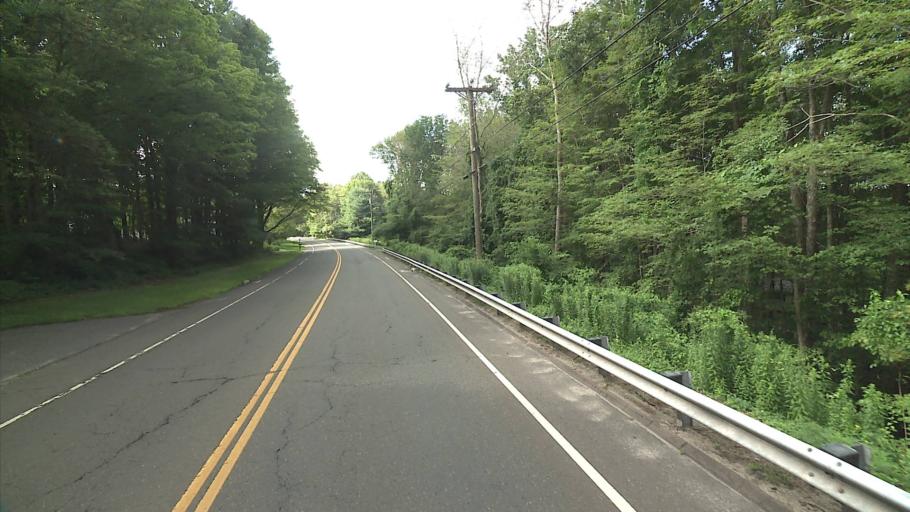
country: US
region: Connecticut
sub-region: Middlesex County
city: Clinton
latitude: 41.3219
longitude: -72.4943
